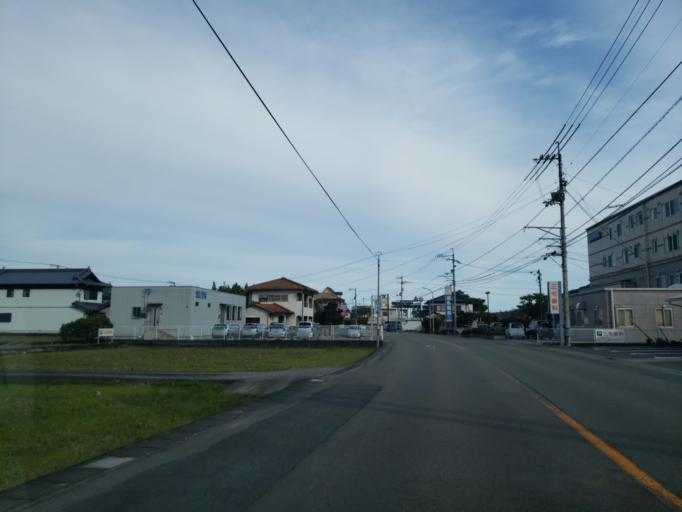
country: JP
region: Tokushima
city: Wakimachi
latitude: 34.0653
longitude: 134.1747
